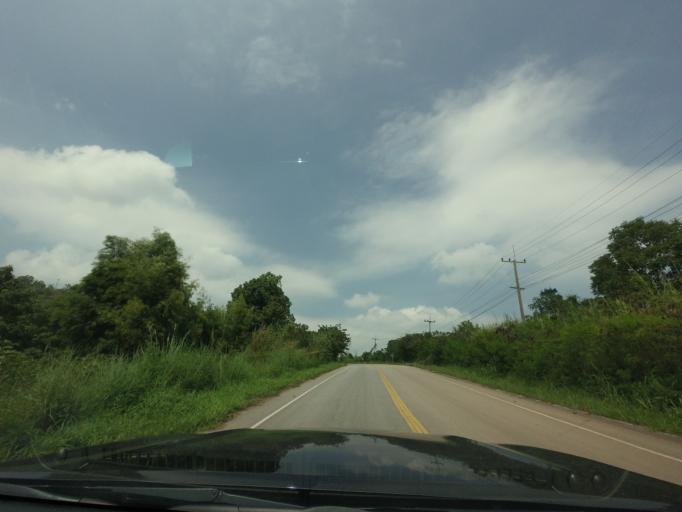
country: TH
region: Loei
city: Phu Ruea
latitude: 17.5047
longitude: 101.4644
